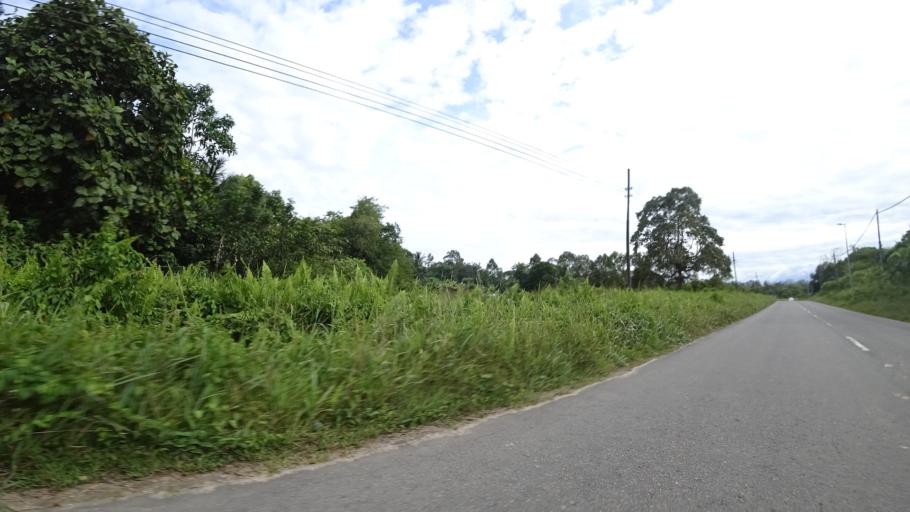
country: BN
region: Brunei and Muara
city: Bandar Seri Begawan
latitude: 4.8418
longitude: 114.9518
